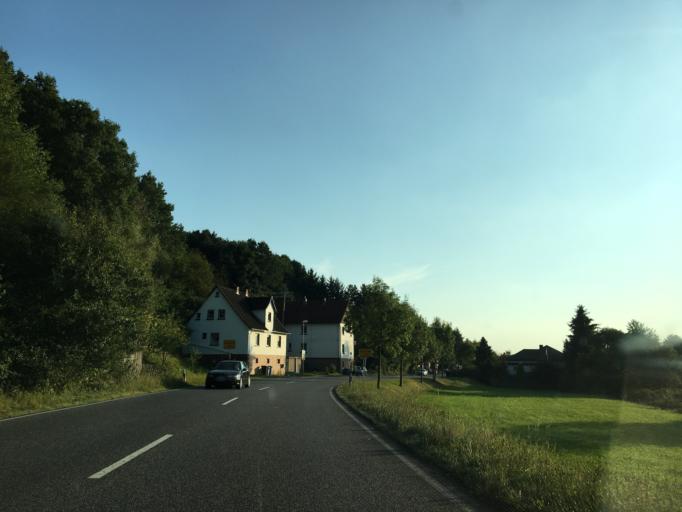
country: DE
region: Hesse
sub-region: Regierungsbezirk Giessen
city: Munchhausen
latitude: 50.9662
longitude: 8.7231
